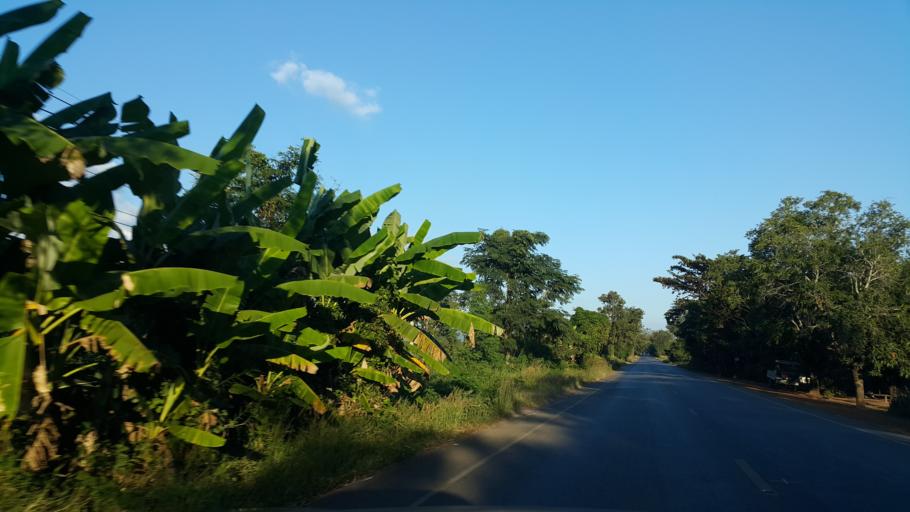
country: TH
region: Sukhothai
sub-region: Amphoe Si Satchanalai
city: Si Satchanalai
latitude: 17.5449
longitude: 99.8359
